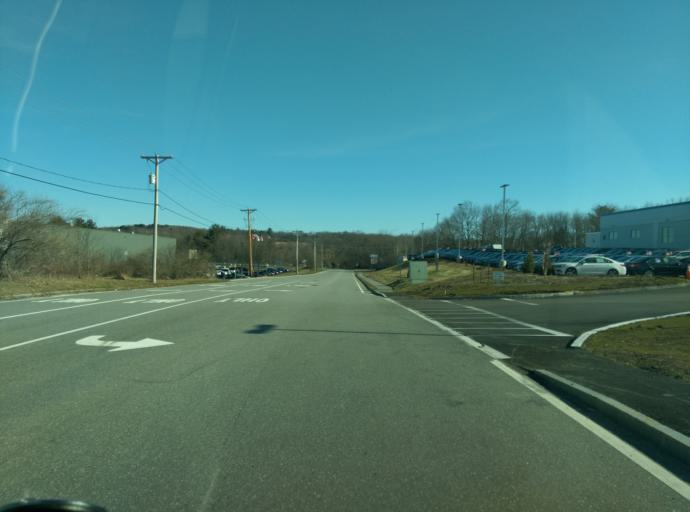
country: US
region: Massachusetts
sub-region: Essex County
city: Haverhill
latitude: 42.7844
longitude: -71.1197
